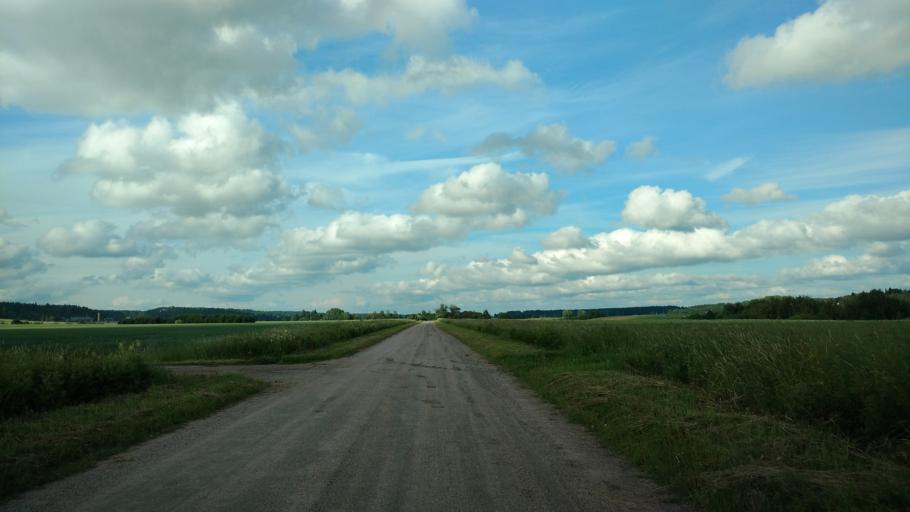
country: FI
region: Varsinais-Suomi
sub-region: Salo
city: Salo
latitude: 60.4033
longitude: 23.1572
